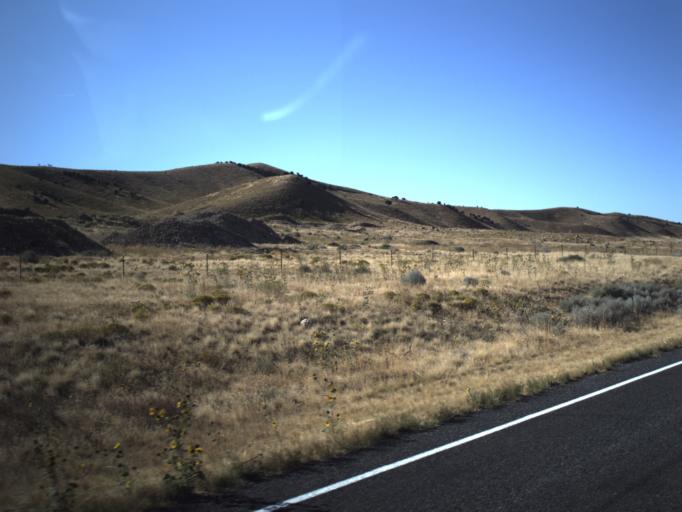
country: US
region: Utah
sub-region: Millard County
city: Delta
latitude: 39.4509
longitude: -112.3065
